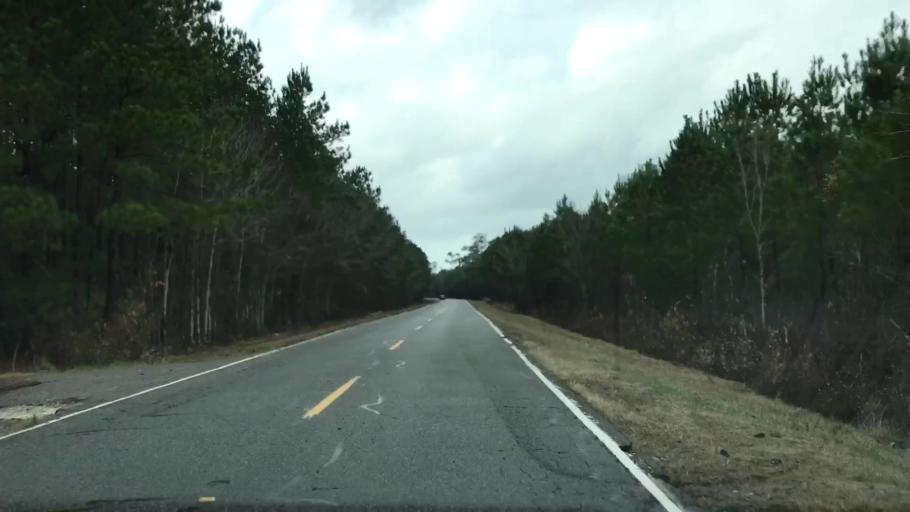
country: US
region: South Carolina
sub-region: Georgetown County
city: Murrells Inlet
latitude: 33.6303
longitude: -79.2478
